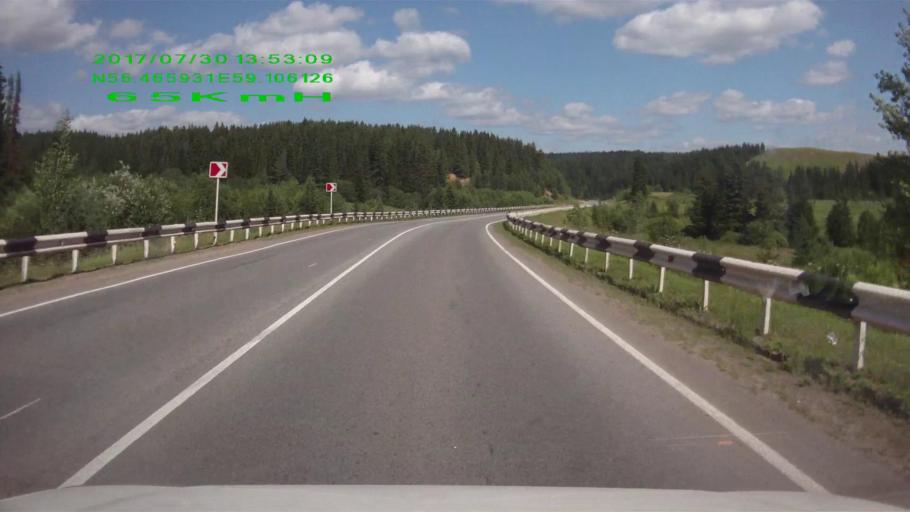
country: RU
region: Sverdlovsk
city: Mikhaylovsk
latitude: 56.4662
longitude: 59.1077
